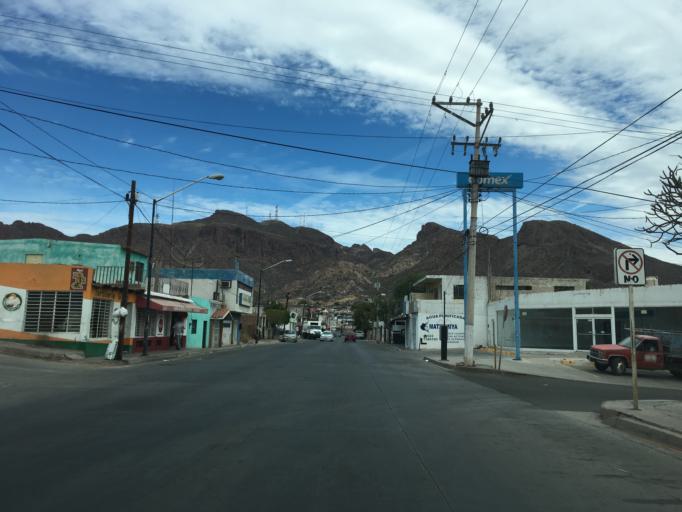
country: MX
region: Sonora
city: Heroica Guaymas
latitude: 27.9199
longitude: -110.9027
